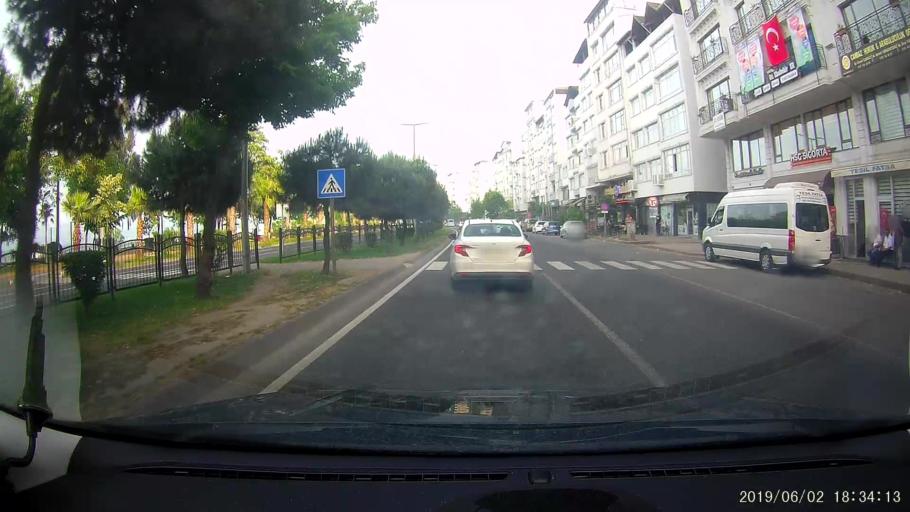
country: TR
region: Ordu
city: Fatsa
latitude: 41.0305
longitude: 37.5021
